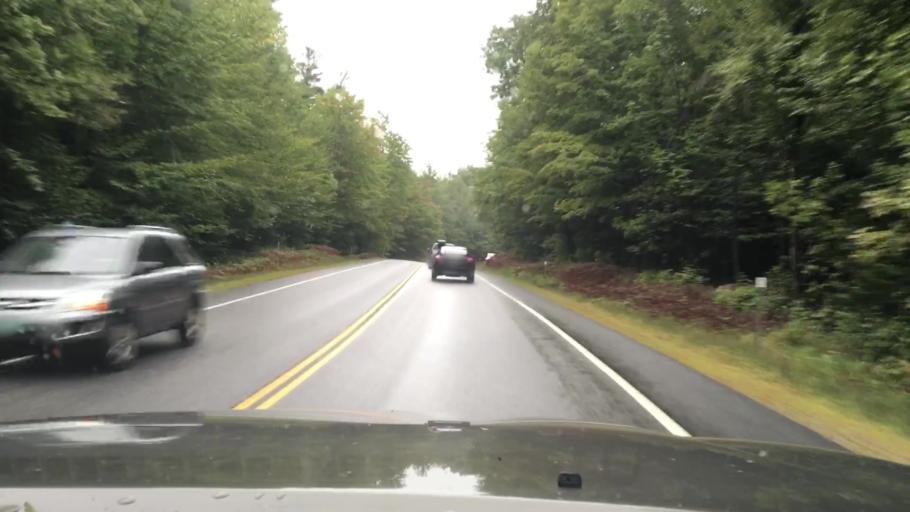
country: US
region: New Hampshire
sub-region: Cheshire County
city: Harrisville
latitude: 43.0659
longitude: -72.0670
